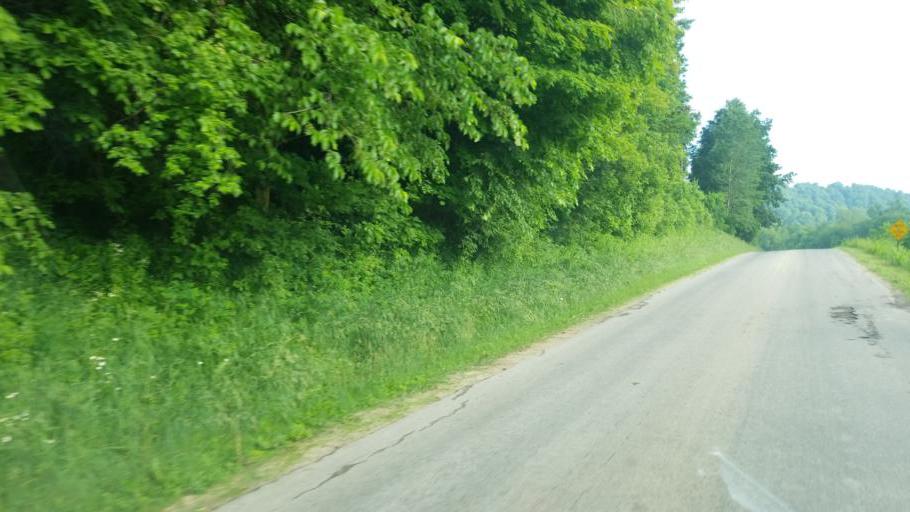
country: US
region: Wisconsin
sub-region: Vernon County
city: Hillsboro
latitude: 43.5960
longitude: -90.3669
